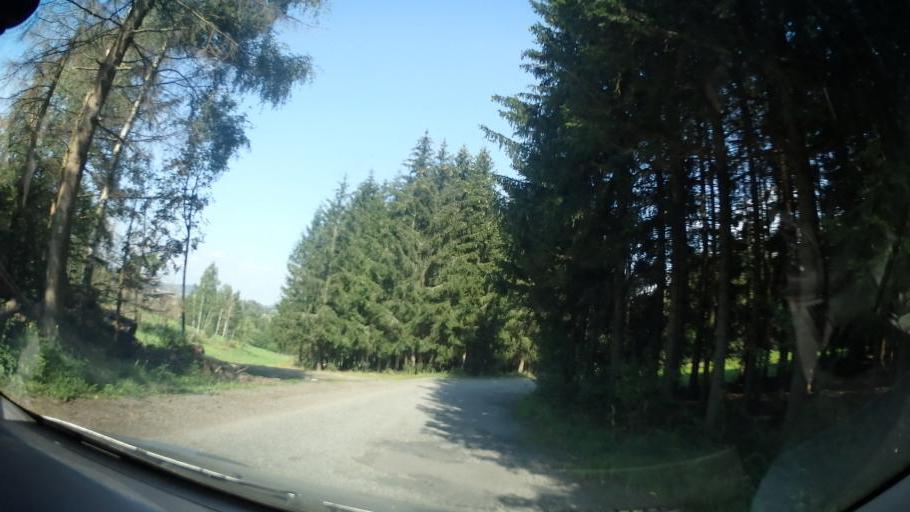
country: CZ
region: South Moravian
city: Olesnice
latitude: 49.5562
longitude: 16.3502
